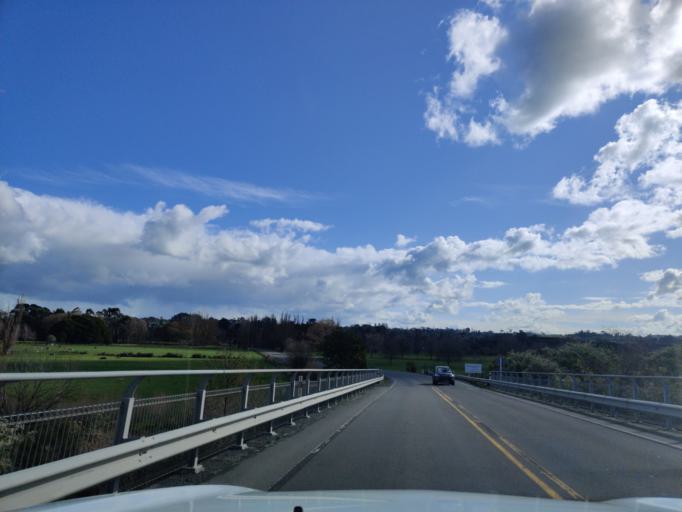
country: NZ
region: Manawatu-Wanganui
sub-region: Palmerston North City
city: Palmerston North
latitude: -40.2814
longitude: 175.7707
